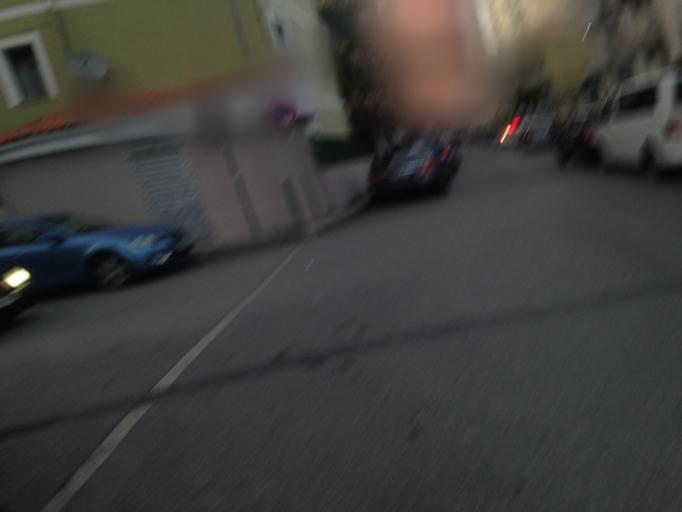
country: AL
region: Tirane
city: Tirana
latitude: 41.3153
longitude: 19.8081
